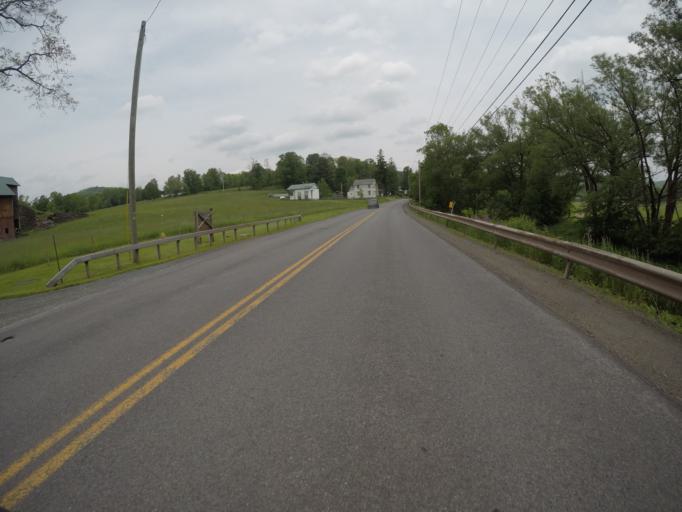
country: US
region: New York
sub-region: Delaware County
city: Delhi
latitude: 42.2594
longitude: -74.7914
